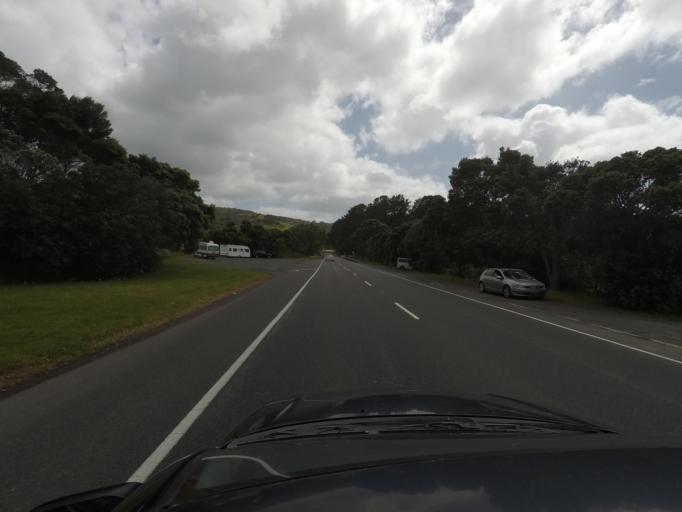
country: NZ
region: Auckland
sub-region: Auckland
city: Warkworth
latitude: -36.5628
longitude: 174.6960
